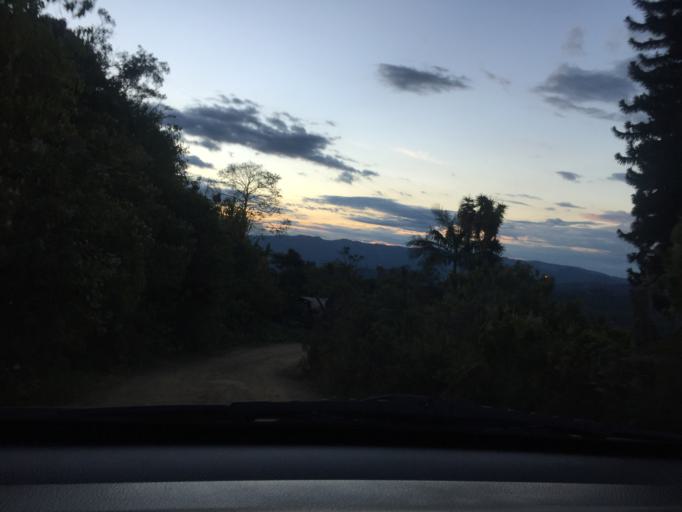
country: CO
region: Cundinamarca
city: Zipacon
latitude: 4.7052
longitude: -74.4095
